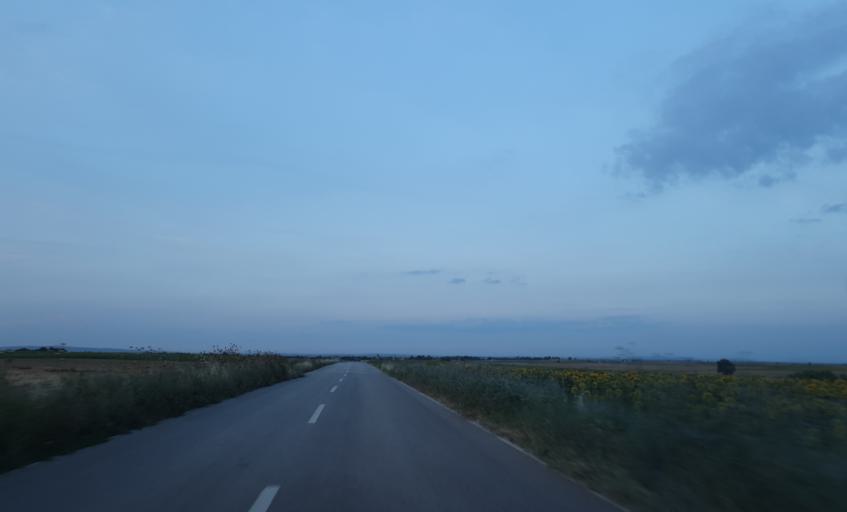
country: TR
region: Tekirdag
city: Beyazkoy
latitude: 41.4268
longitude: 27.6797
